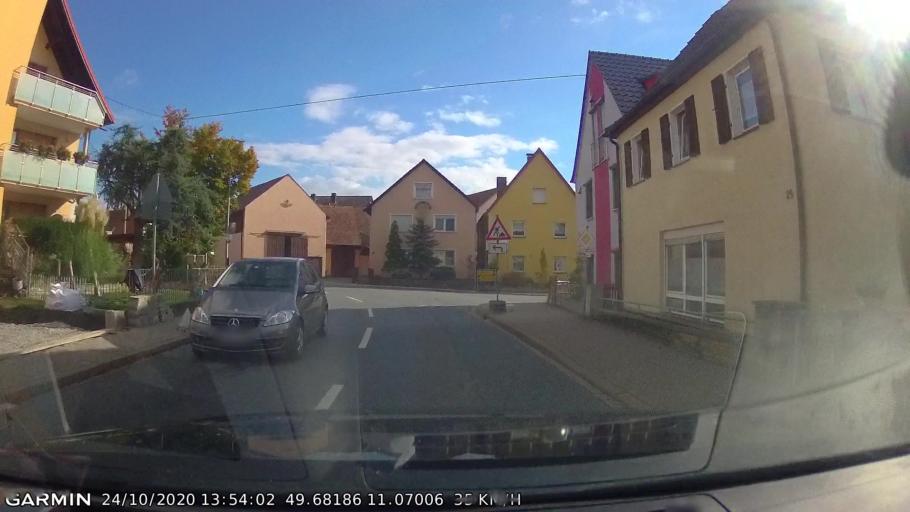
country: DE
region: Bavaria
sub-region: Upper Franconia
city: Poxdorf
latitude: 49.6818
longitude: 11.0701
